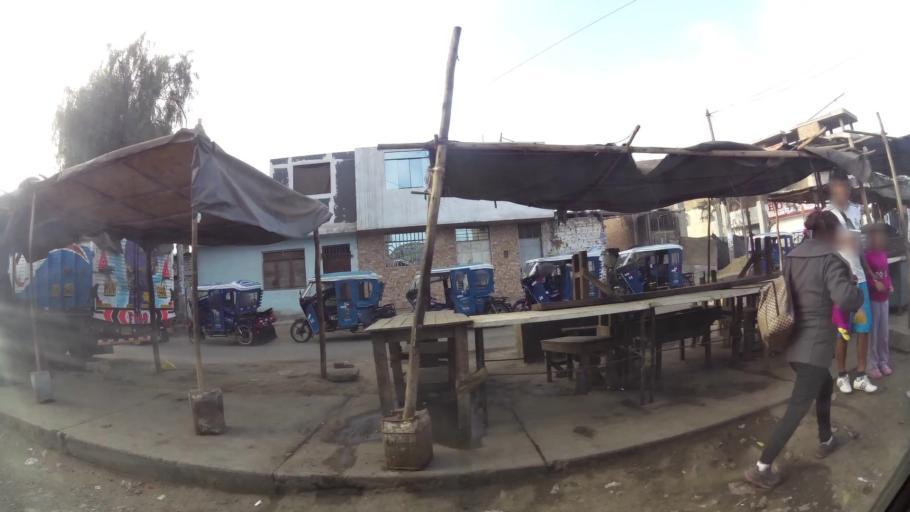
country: PE
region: La Libertad
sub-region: Provincia de Trujillo
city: La Esperanza
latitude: -8.0890
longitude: -79.0252
